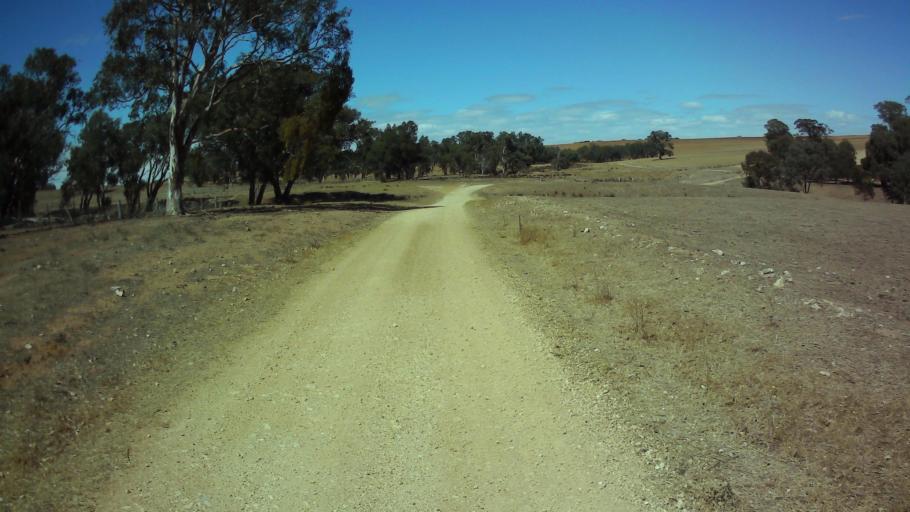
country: AU
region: New South Wales
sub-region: Young
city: Young
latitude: -34.0438
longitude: 148.4271
